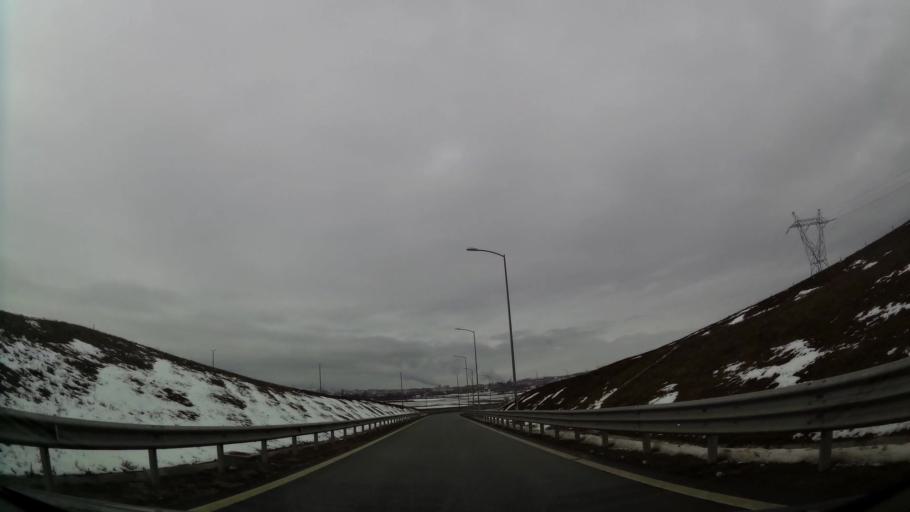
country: XK
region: Pristina
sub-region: Kosovo Polje
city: Kosovo Polje
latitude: 42.6222
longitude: 21.1177
